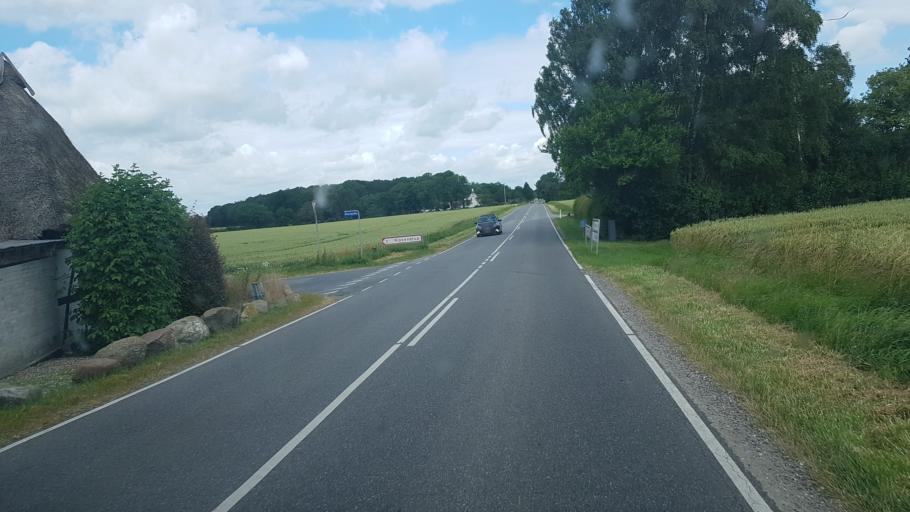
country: DK
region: South Denmark
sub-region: Kerteminde Kommune
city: Kerteminde
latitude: 55.4058
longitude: 10.7240
